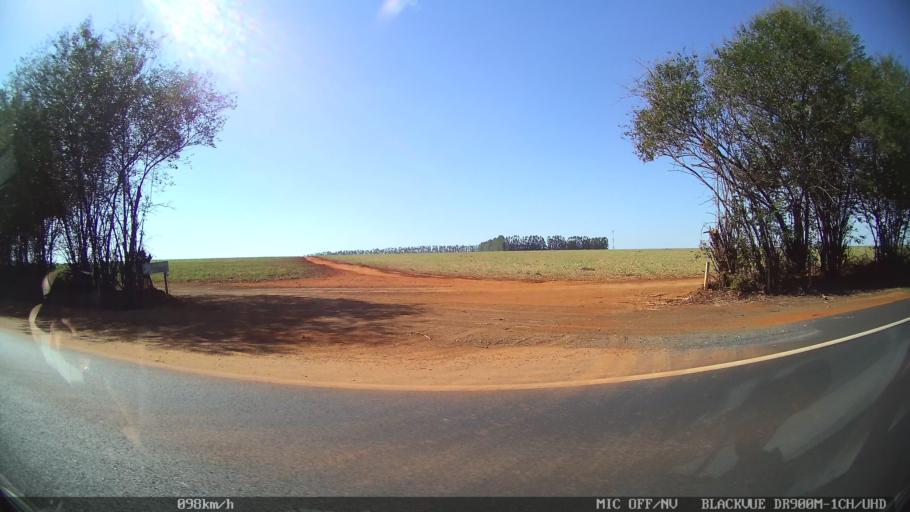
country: BR
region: Sao Paulo
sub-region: Batatais
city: Batatais
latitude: -20.7436
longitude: -47.5312
